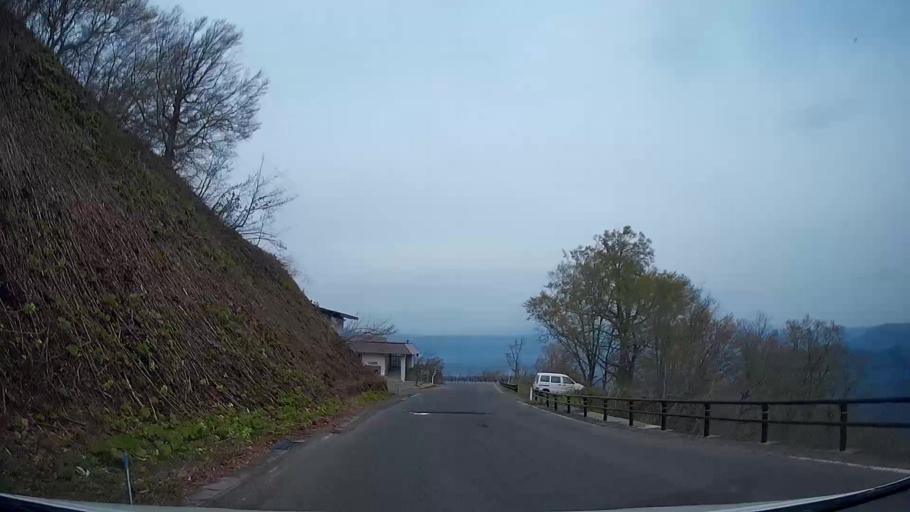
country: JP
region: Akita
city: Hanawa
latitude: 40.4082
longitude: 140.8647
